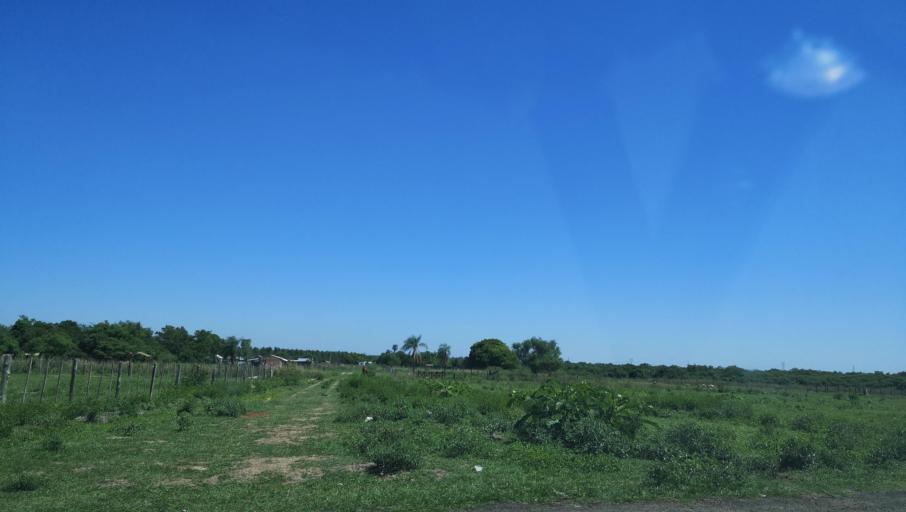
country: PY
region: Caaguazu
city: Carayao
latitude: -25.1919
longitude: -56.4048
